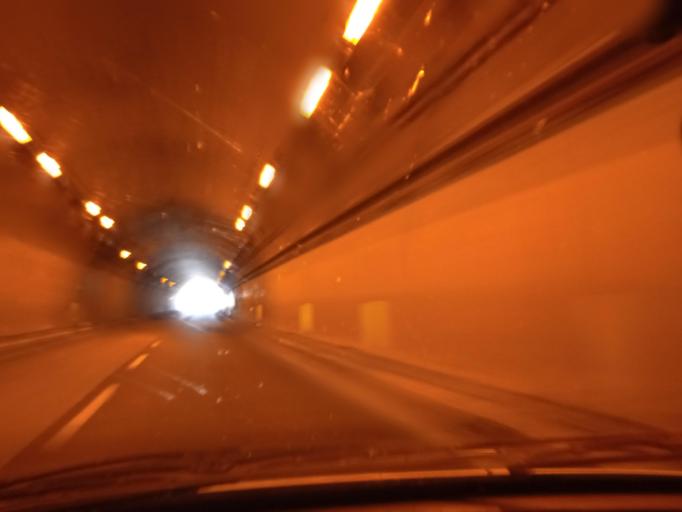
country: IT
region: Sicily
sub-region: Messina
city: Torrenova
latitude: 38.0755
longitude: 14.6606
